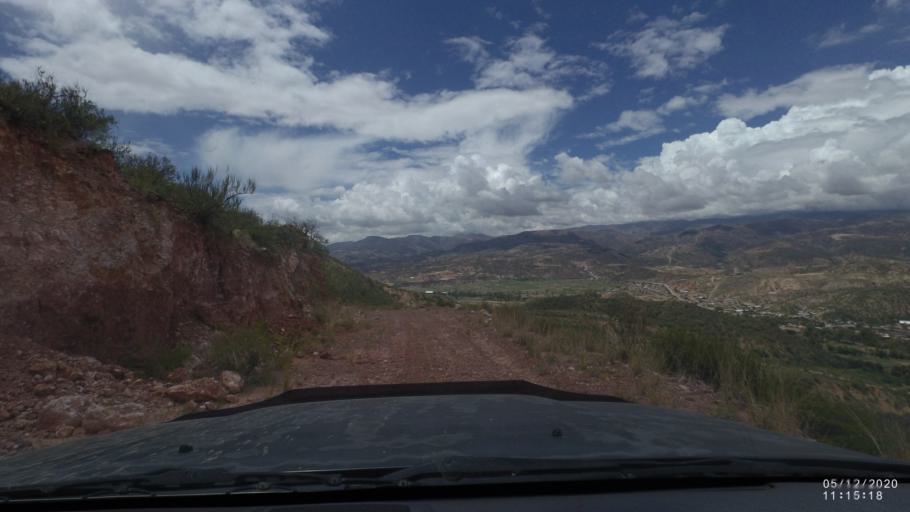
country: BO
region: Cochabamba
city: Sipe Sipe
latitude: -17.5491
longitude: -66.3300
